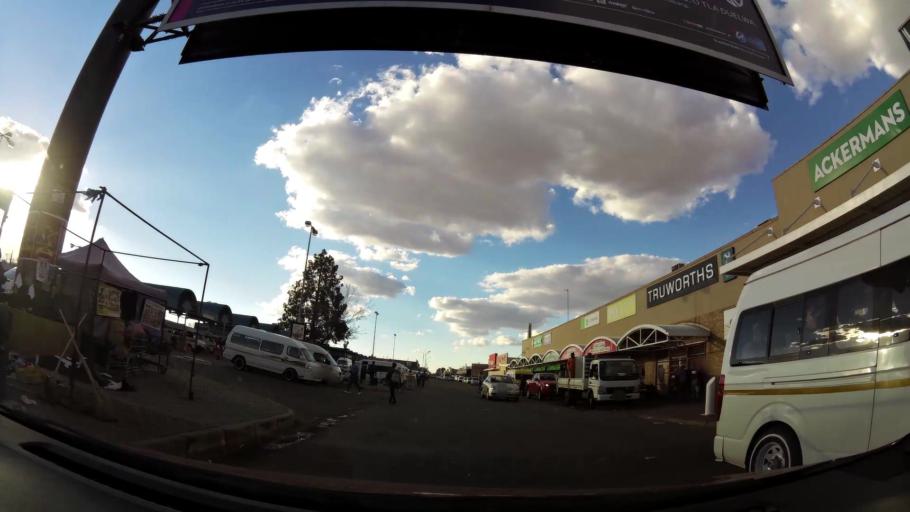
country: ZA
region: North-West
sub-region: Dr Kenneth Kaunda District Municipality
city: Potchefstroom
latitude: -26.7134
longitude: 27.1012
